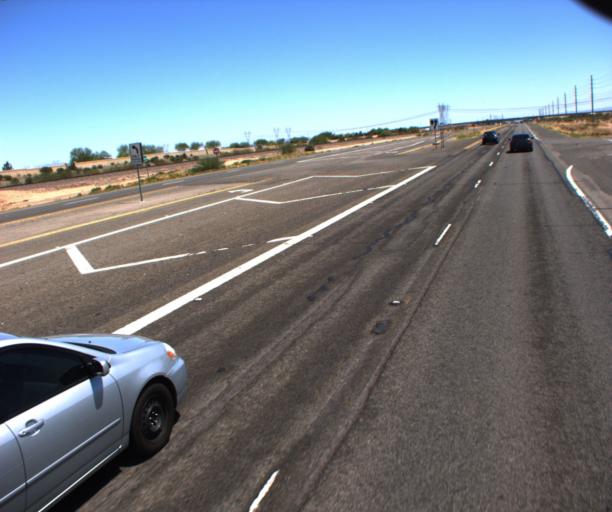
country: US
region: Arizona
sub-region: Maricopa County
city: Sun City West
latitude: 33.6915
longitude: -112.4183
